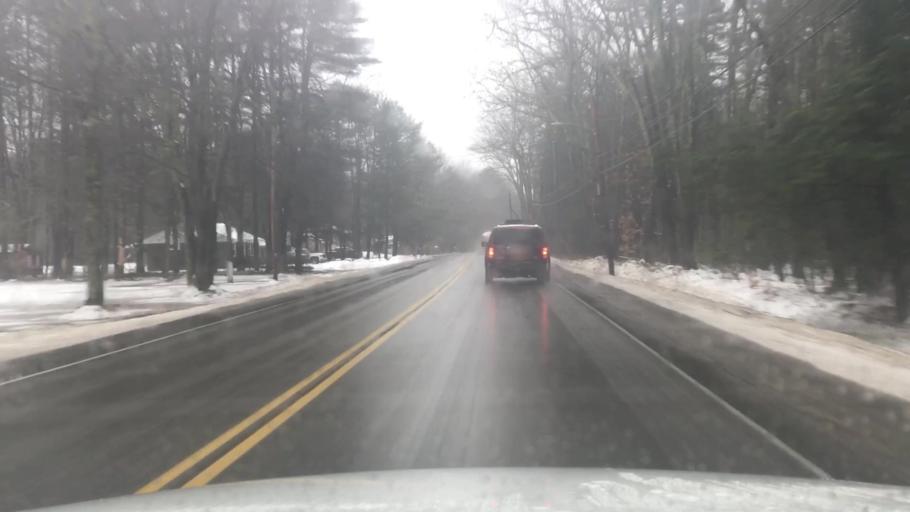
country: US
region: Maine
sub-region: Cumberland County
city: Westbrook
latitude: 43.6384
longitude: -70.3964
